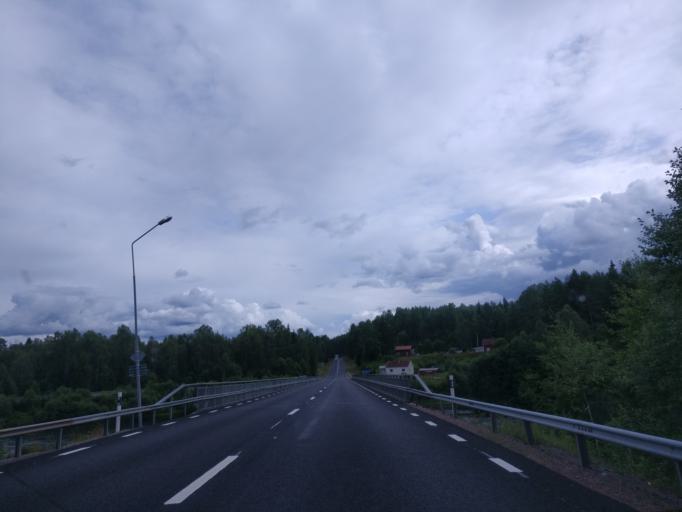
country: SE
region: Vaermland
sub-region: Hagfors Kommun
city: Ekshaerad
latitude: 60.0620
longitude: 13.5509
